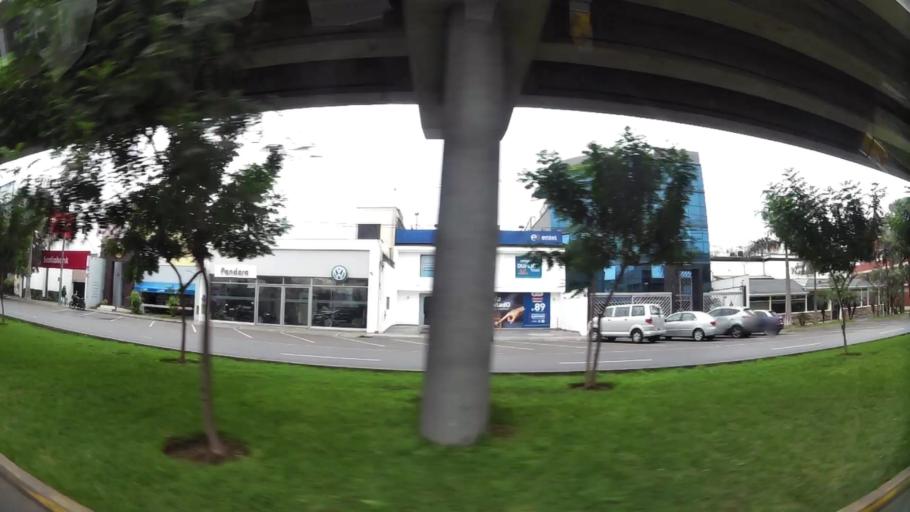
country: PE
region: Lima
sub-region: Lima
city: San Luis
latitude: -12.0932
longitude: -77.0029
